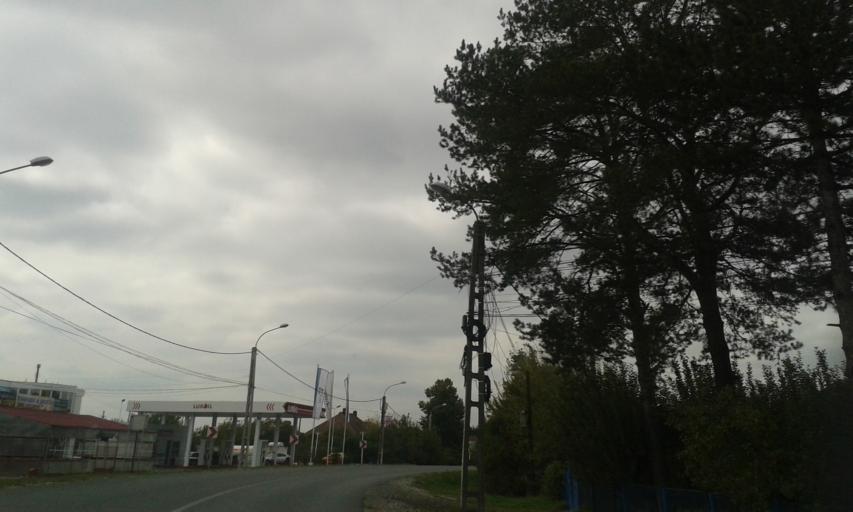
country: RO
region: Gorj
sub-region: Comuna Turcinesti
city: Turcinesti
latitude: 45.0774
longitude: 23.3109
